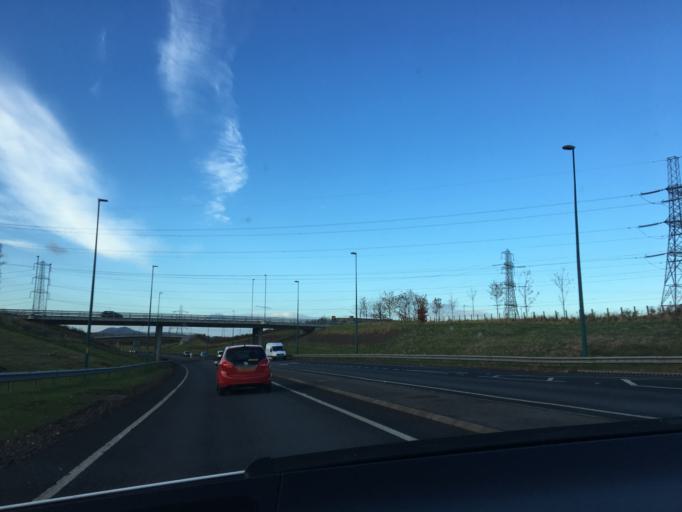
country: GB
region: Scotland
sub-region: Midlothian
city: Dalkeith
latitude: 55.9098
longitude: -3.0445
